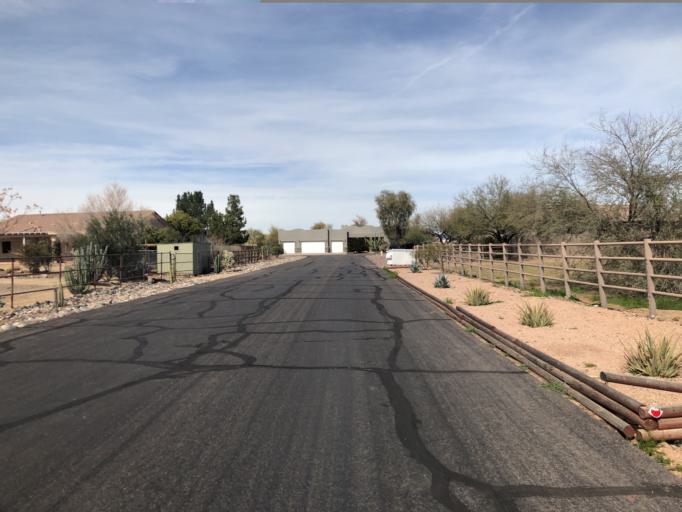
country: US
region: Arizona
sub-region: Maricopa County
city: Anthem
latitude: 33.8381
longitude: -112.0703
